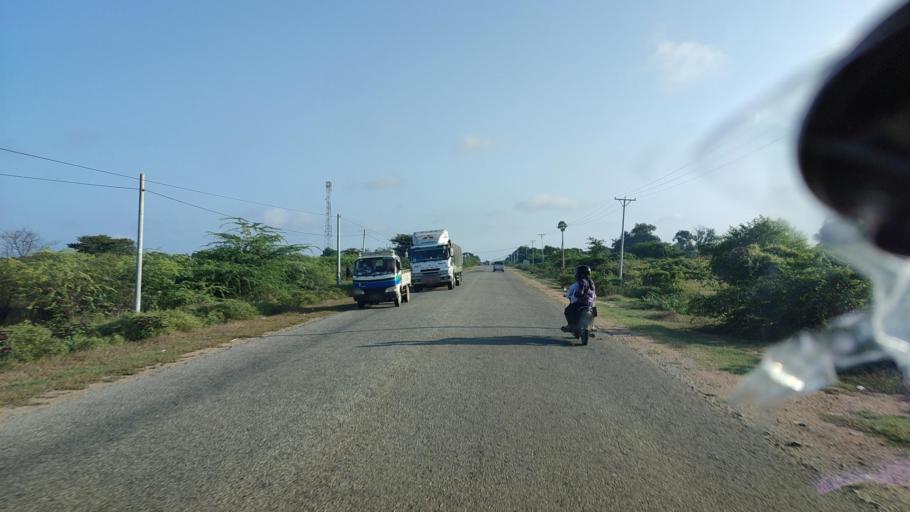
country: MM
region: Mandalay
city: Yamethin
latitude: 20.6102
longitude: 96.0710
